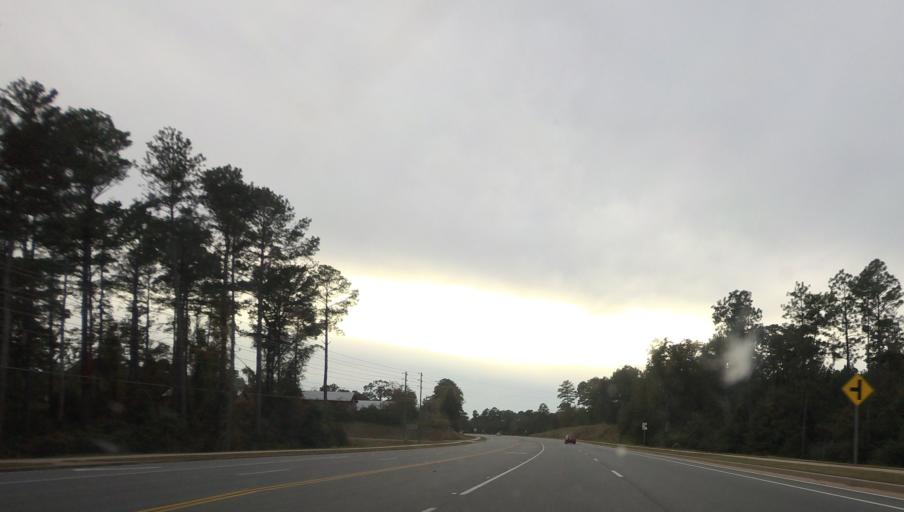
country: US
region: Georgia
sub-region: Houston County
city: Perry
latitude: 32.4973
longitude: -83.6742
